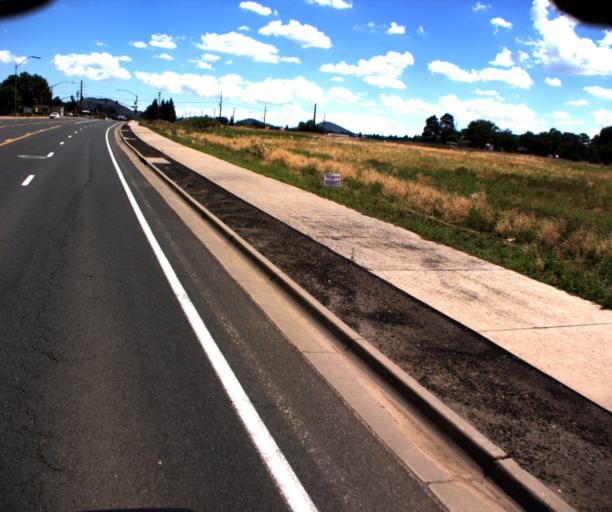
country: US
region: Arizona
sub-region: Coconino County
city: Flagstaff
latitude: 35.2070
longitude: -111.6117
